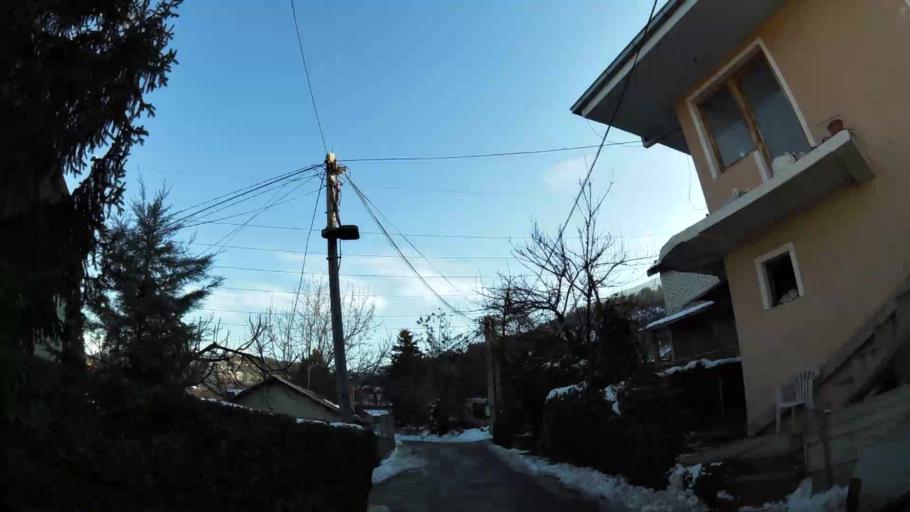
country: MK
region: Karpos
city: Skopje
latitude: 41.9905
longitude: 21.4022
